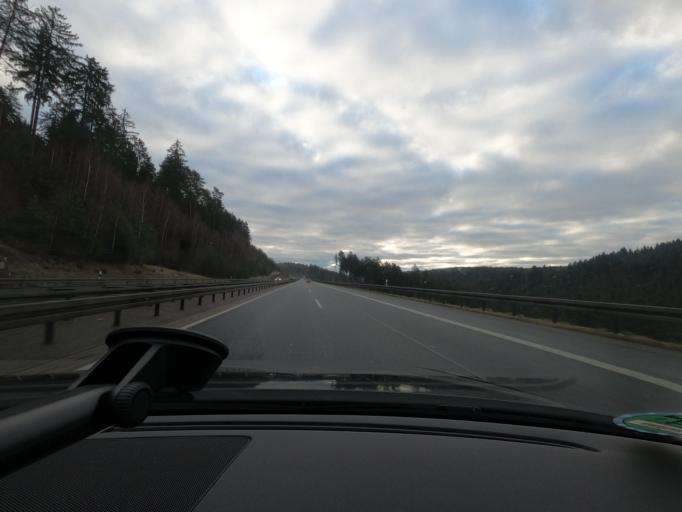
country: DE
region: Thuringia
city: Bischofrod
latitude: 50.5942
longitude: 10.6473
